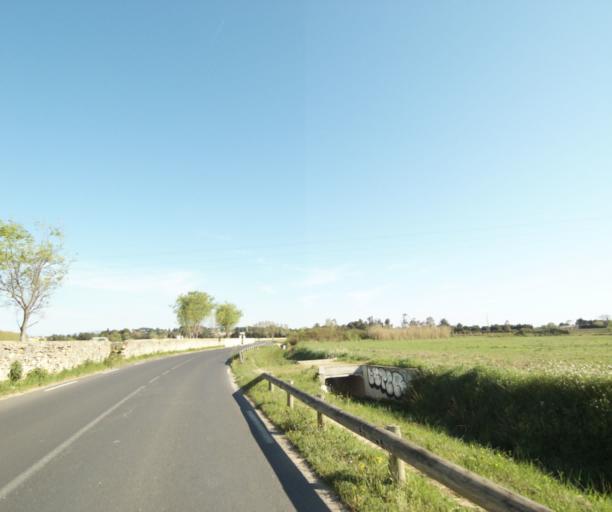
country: FR
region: Languedoc-Roussillon
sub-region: Departement de l'Herault
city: Castelnau-le-Lez
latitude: 43.6266
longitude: 3.9210
